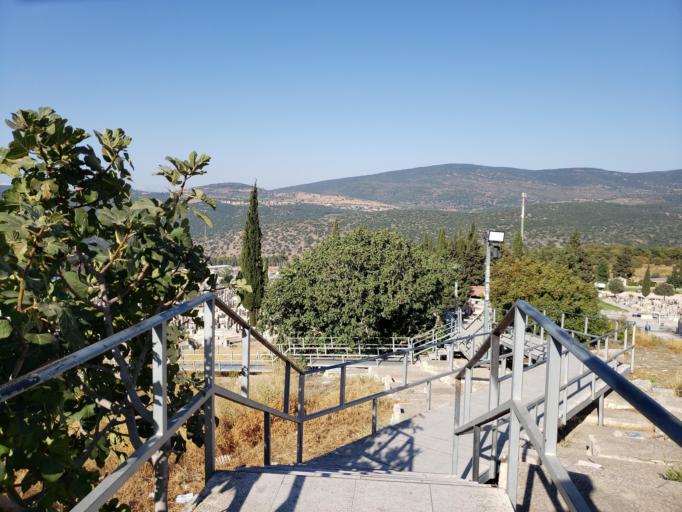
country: IL
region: Northern District
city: Safed
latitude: 32.9679
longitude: 35.4882
